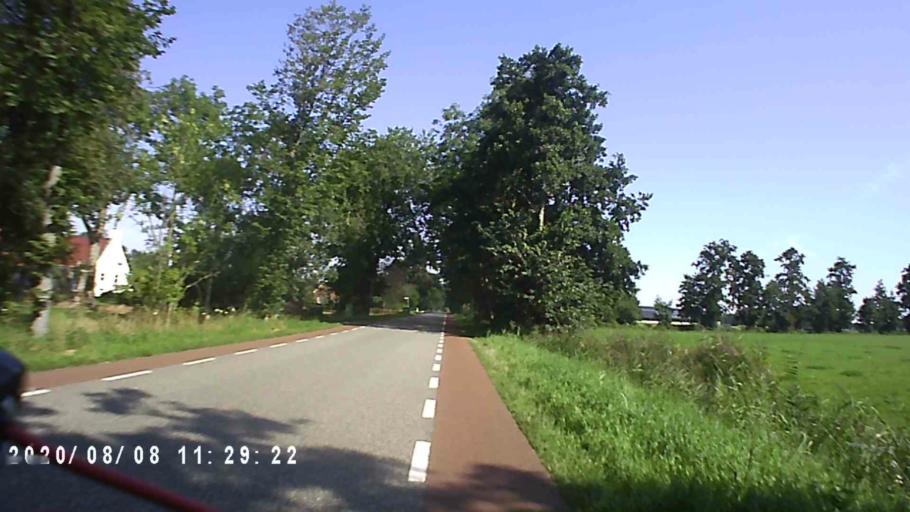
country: NL
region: Groningen
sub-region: Gemeente Leek
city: Leek
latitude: 53.1960
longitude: 6.3866
